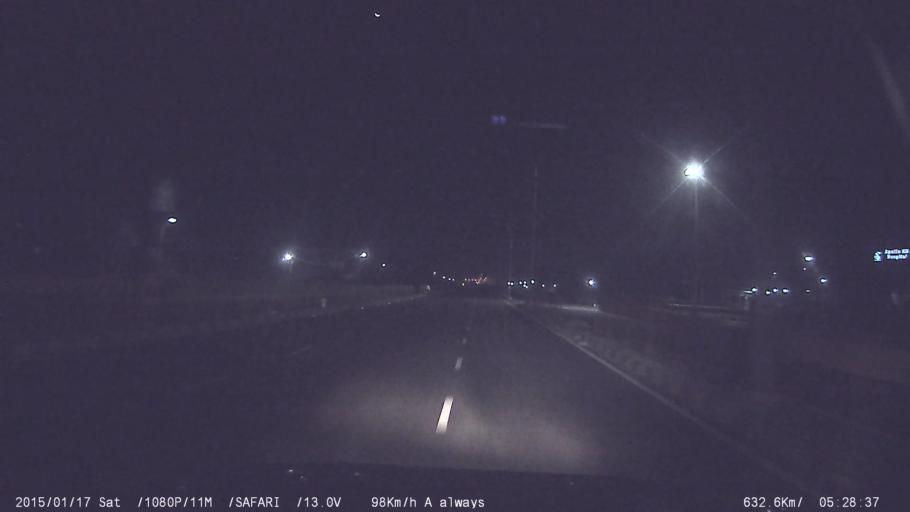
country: IN
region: Tamil Nadu
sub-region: Vellore
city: Arcot
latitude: 12.9241
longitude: 79.2747
